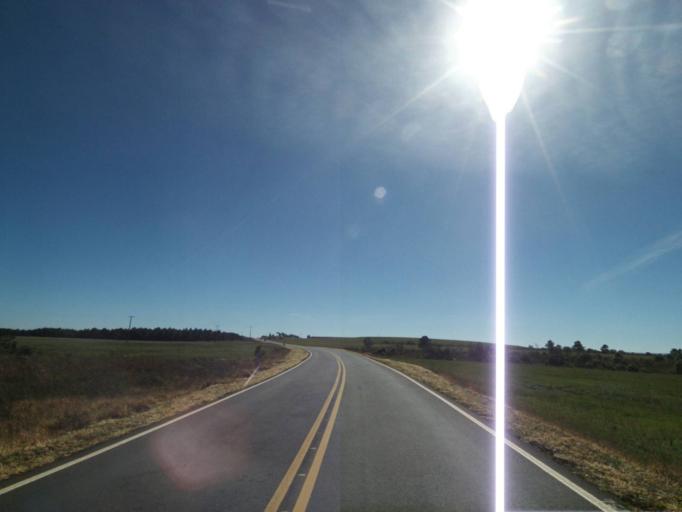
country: BR
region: Parana
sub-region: Castro
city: Castro
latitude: -24.7011
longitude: -50.1934
